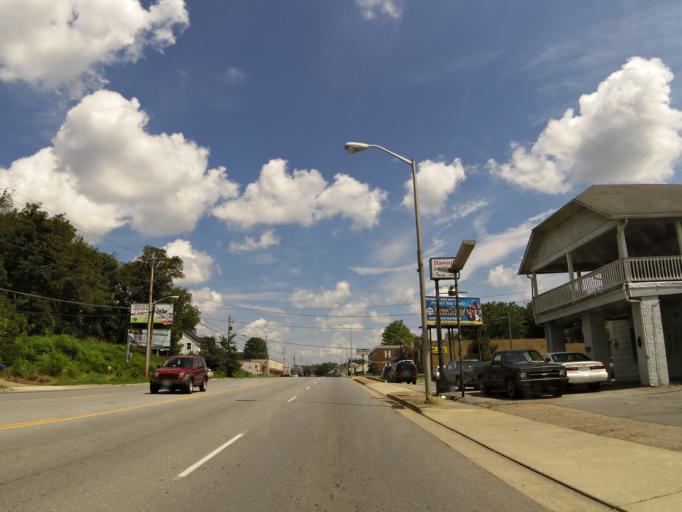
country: US
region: Virginia
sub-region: Washington County
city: Abingdon
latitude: 36.7062
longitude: -81.9942
